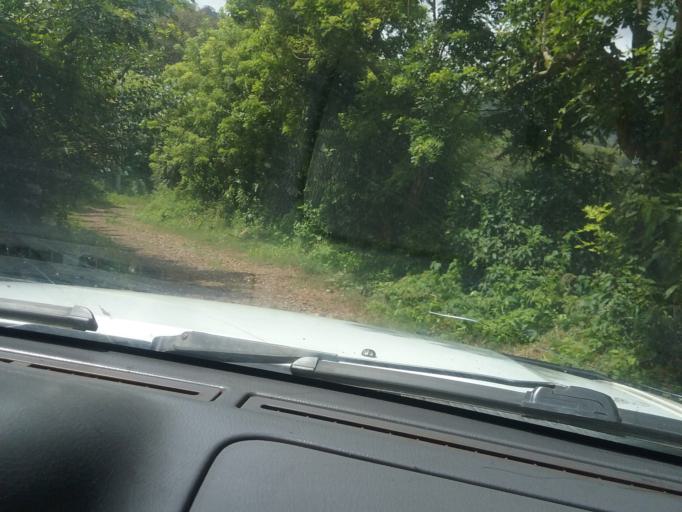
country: NI
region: Matagalpa
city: Matagalpa
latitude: 12.8665
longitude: -85.9121
